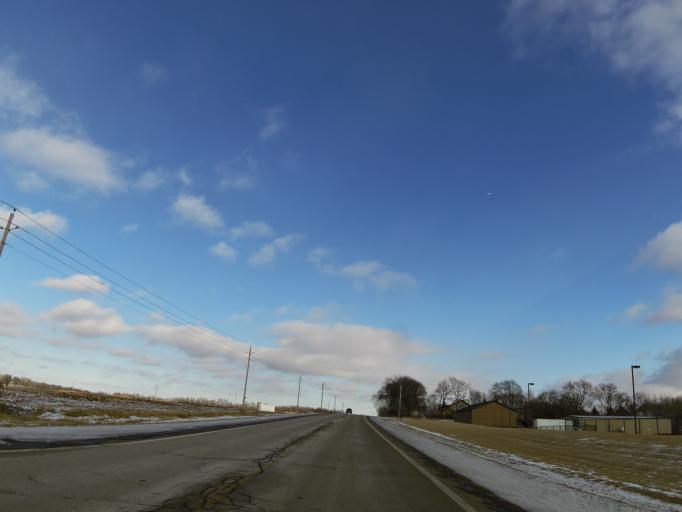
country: US
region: Minnesota
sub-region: Scott County
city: Shakopee
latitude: 44.7465
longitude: -93.4872
